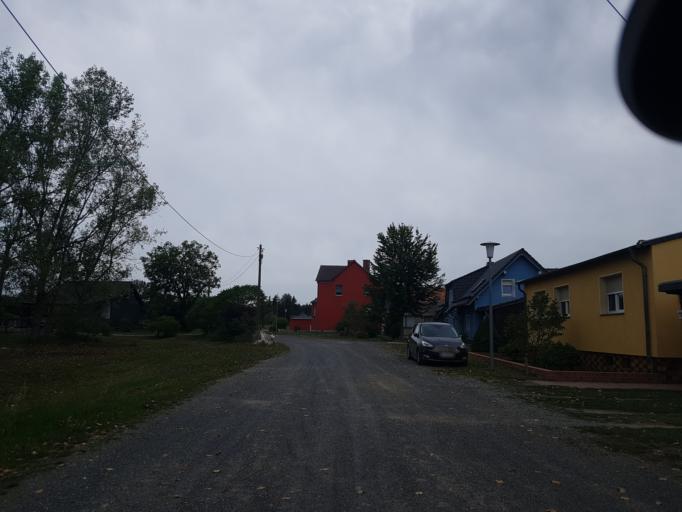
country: DE
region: Brandenburg
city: Finsterwalde
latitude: 51.6087
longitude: 13.6442
